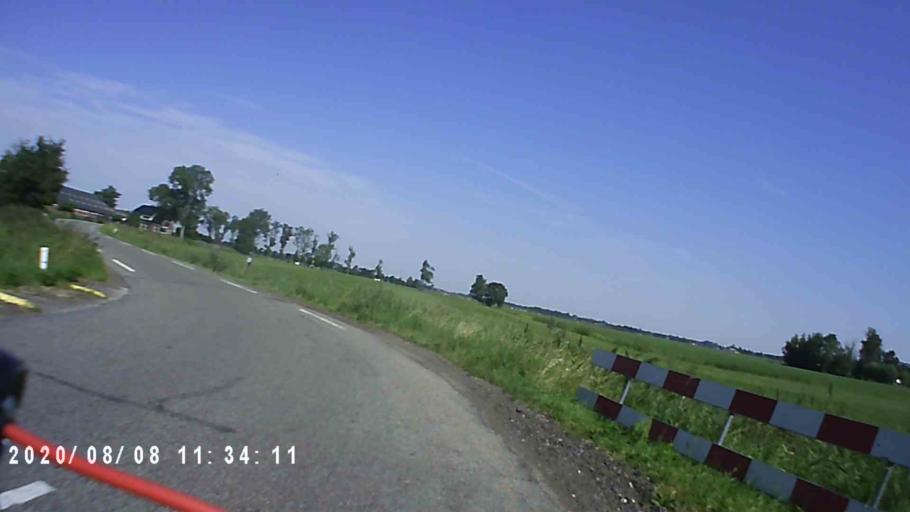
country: NL
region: Groningen
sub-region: Gemeente Zuidhorn
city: Zuidhorn
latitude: 53.2152
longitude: 6.3903
